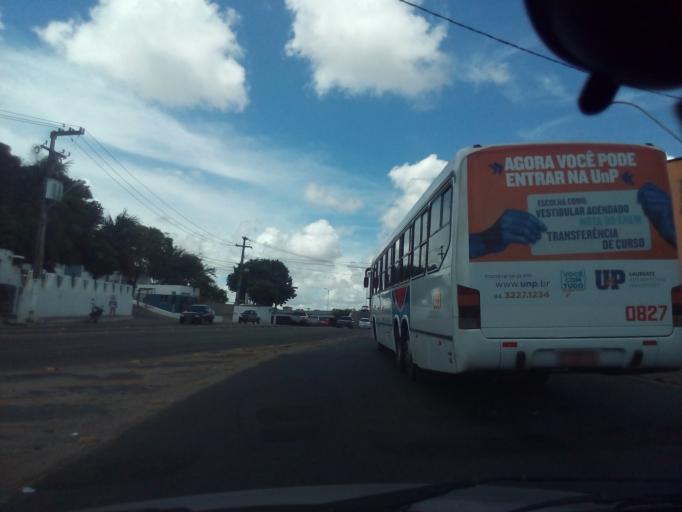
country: BR
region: Rio Grande do Norte
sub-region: Natal
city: Natal
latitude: -5.7988
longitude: -35.2380
